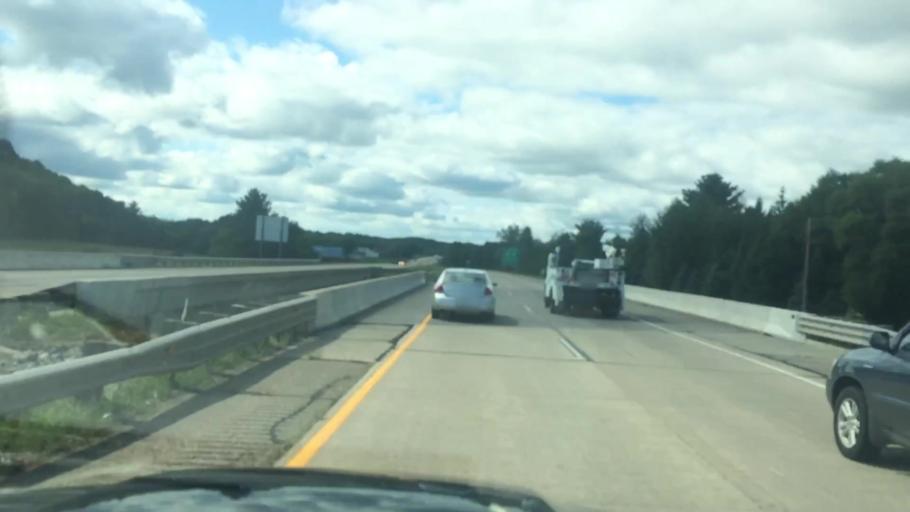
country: US
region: Wisconsin
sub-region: Waupaca County
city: Waupaca
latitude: 44.3408
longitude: -89.0780
